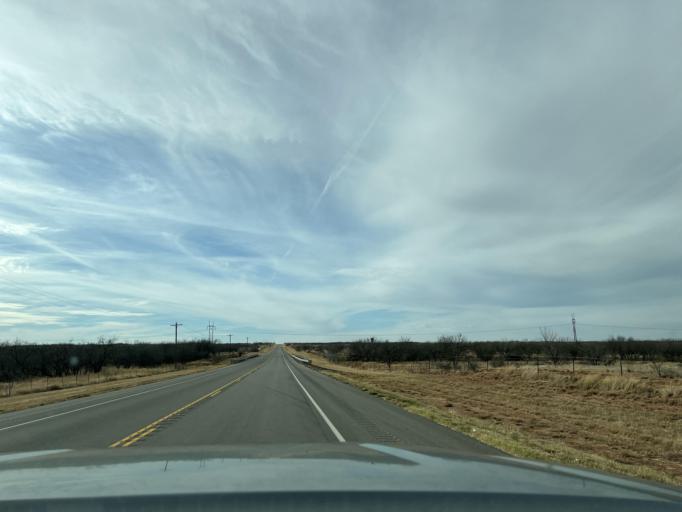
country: US
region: Texas
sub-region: Jones County
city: Anson
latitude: 32.7508
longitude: -99.7277
